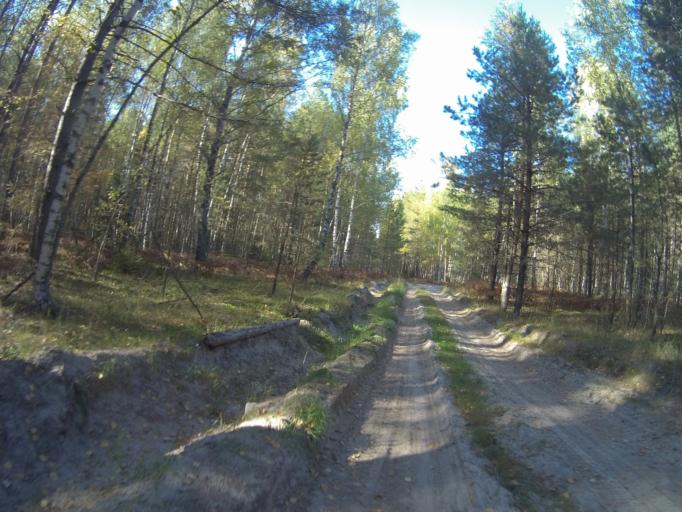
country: RU
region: Vladimir
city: Vorsha
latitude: 55.9066
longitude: 40.1706
